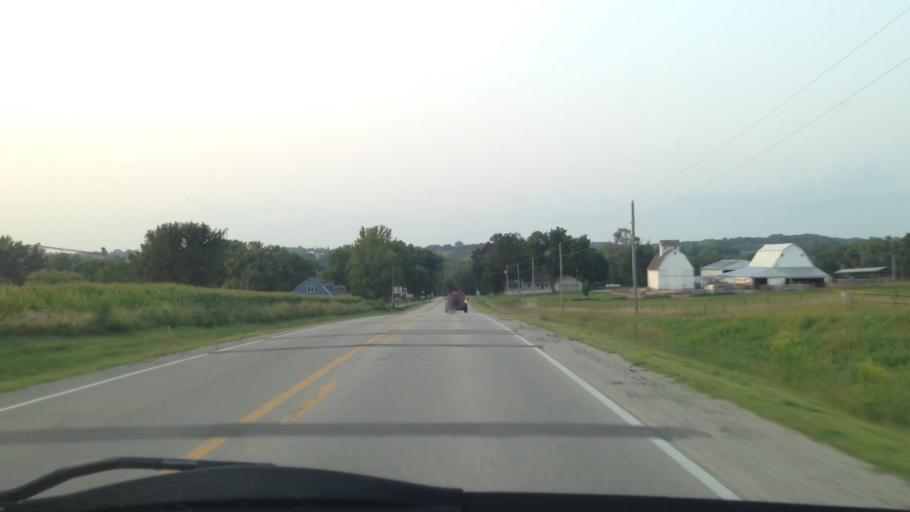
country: US
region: Iowa
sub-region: Linn County
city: Palo
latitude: 42.0855
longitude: -91.8688
